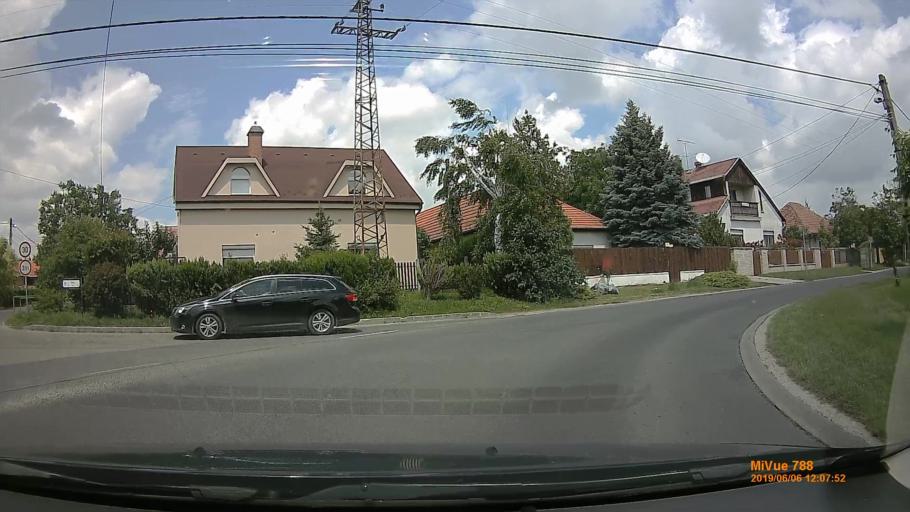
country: HU
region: Pest
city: Kerepes
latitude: 47.5668
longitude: 19.2682
